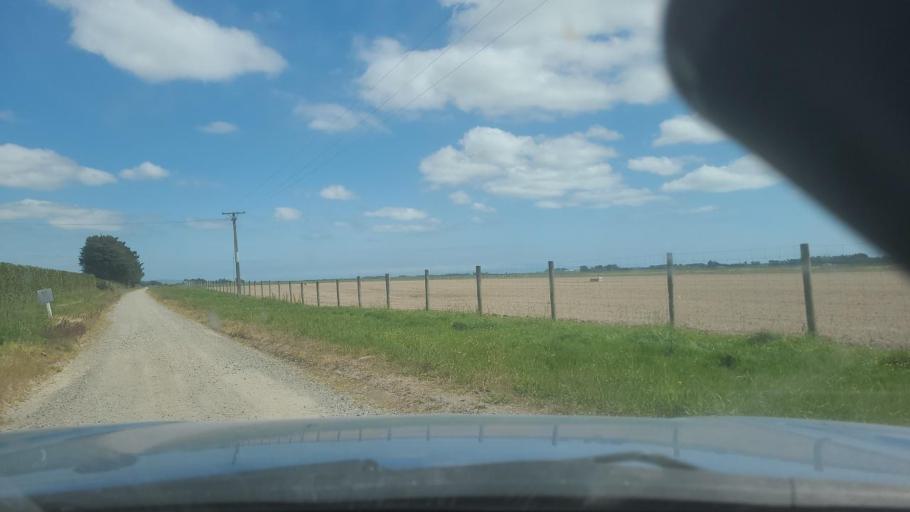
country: NZ
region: Southland
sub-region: Invercargill City
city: Invercargill
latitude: -46.3284
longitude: 168.2594
